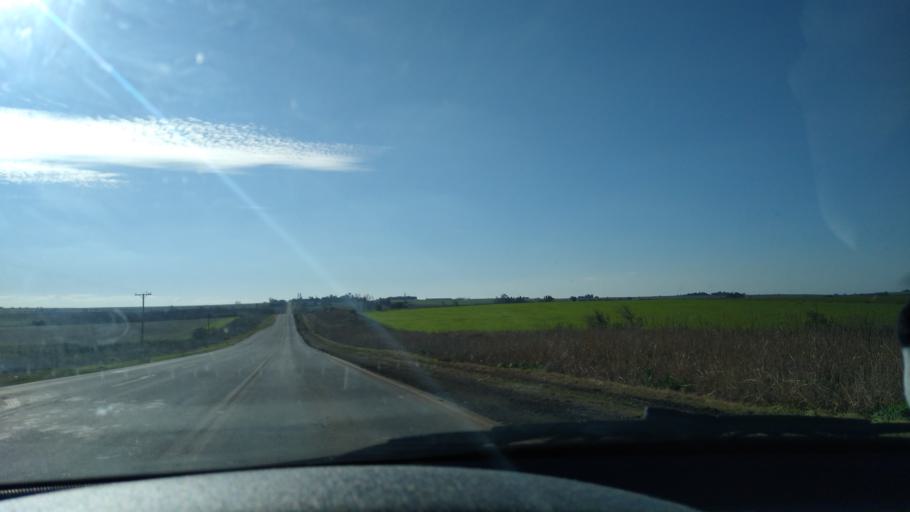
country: AR
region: Entre Rios
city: Aranguren
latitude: -32.3825
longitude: -60.3360
